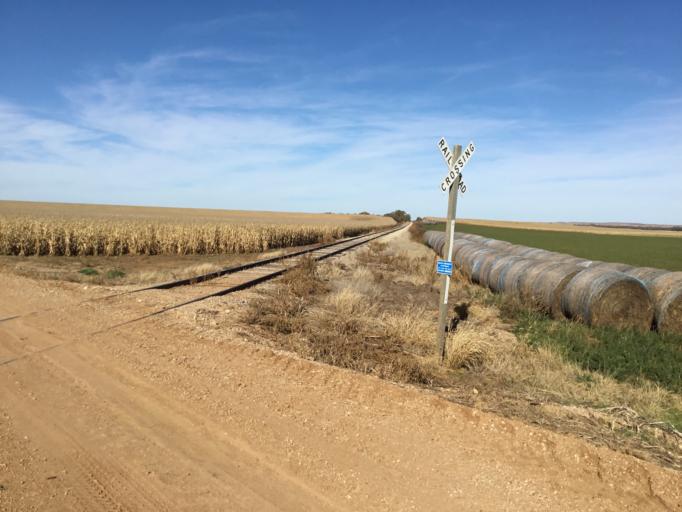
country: US
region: Kansas
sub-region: Lincoln County
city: Lincoln
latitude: 38.9871
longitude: -98.0655
